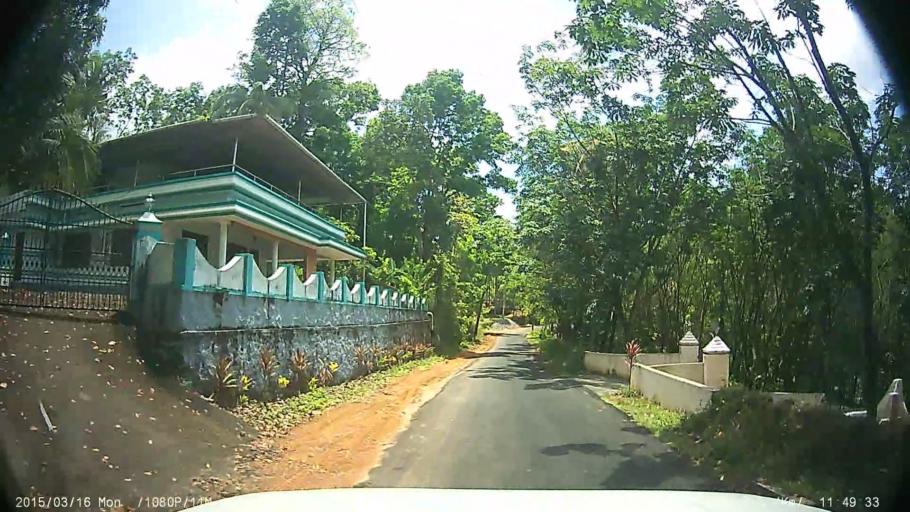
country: IN
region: Kerala
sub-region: Kottayam
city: Palackattumala
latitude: 9.7892
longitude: 76.5496
